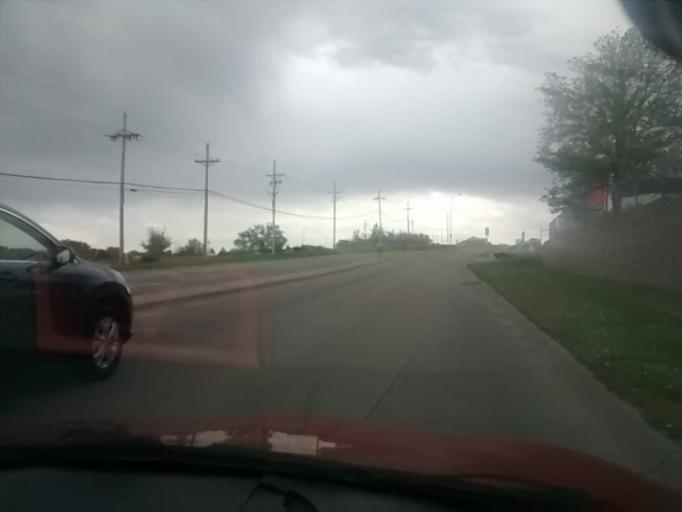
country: US
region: Nebraska
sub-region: Sarpy County
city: Offutt Air Force Base
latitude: 41.1416
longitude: -95.9669
